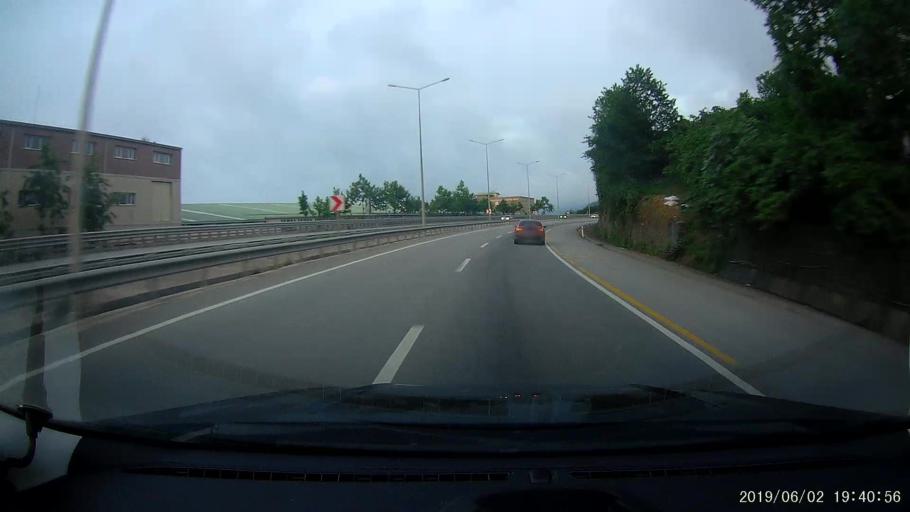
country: TR
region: Giresun
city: Kesap
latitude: 40.9178
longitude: 38.4700
